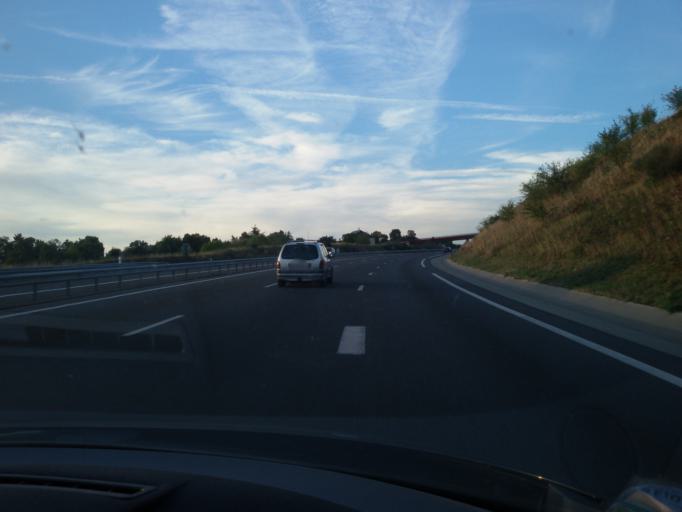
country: FR
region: Midi-Pyrenees
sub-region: Departement de l'Aveyron
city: Severac-le-Chateau
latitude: 44.2447
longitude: 3.0549
